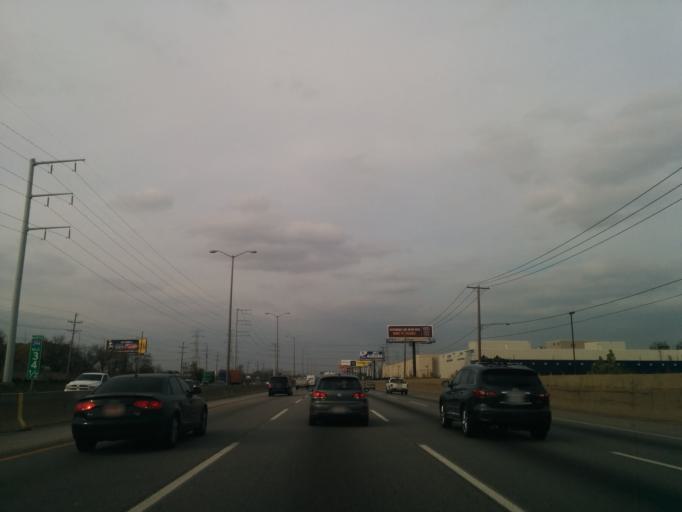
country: US
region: Illinois
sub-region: Cook County
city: Northlake
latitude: 41.9189
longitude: -87.9196
